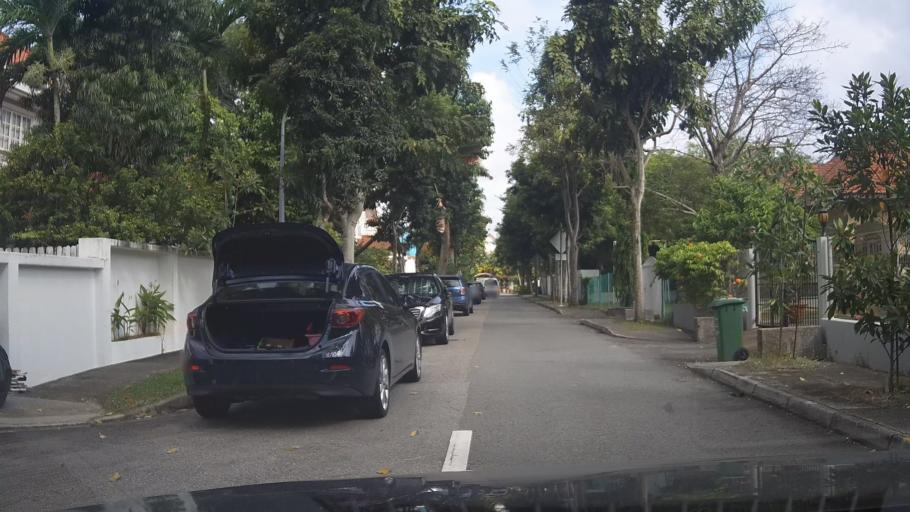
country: SG
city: Singapore
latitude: 1.2976
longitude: 103.8924
